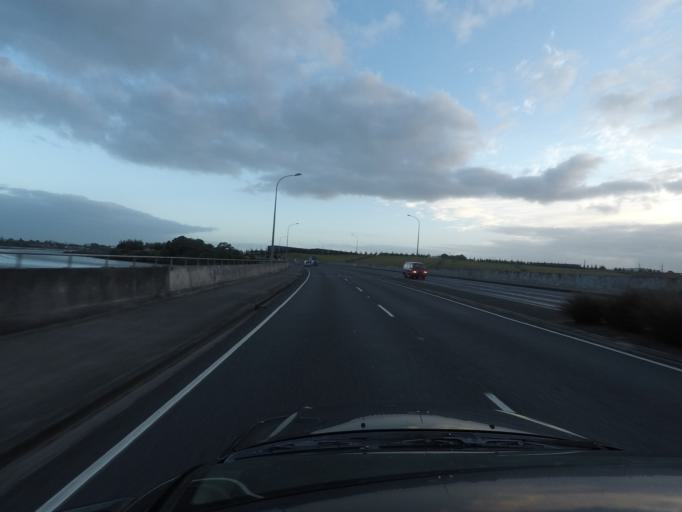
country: NZ
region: Auckland
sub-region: Auckland
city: Manukau City
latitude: -36.9463
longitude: 174.8610
